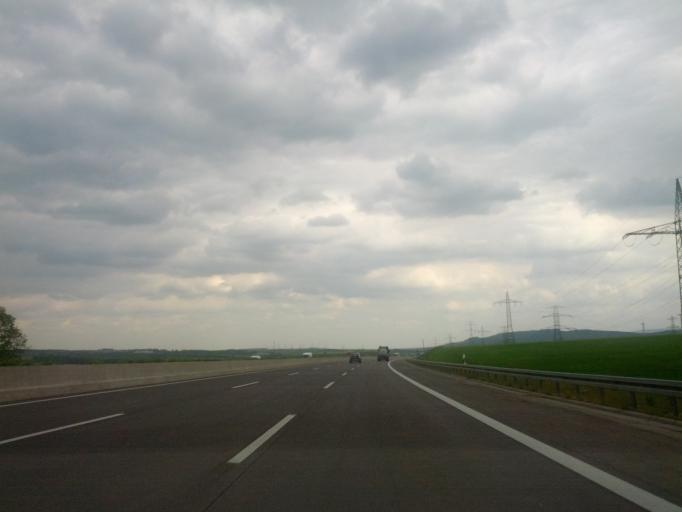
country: DE
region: Thuringia
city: Bischofroda
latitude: 51.0132
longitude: 10.3817
